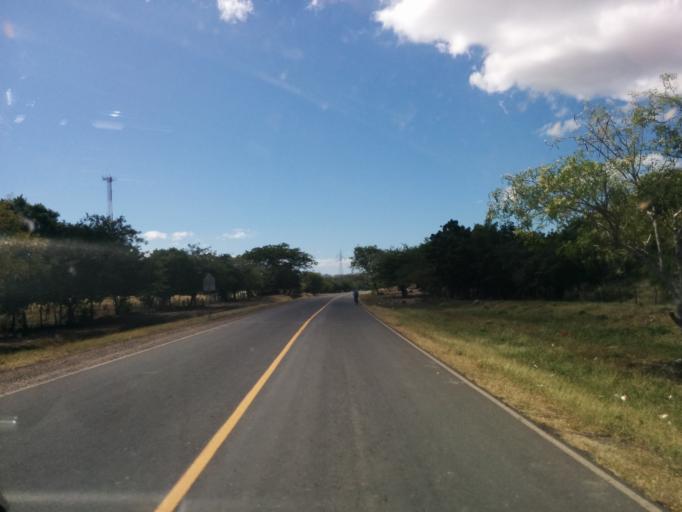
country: NI
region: Matagalpa
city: Ciudad Dario
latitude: 12.8354
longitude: -86.2183
